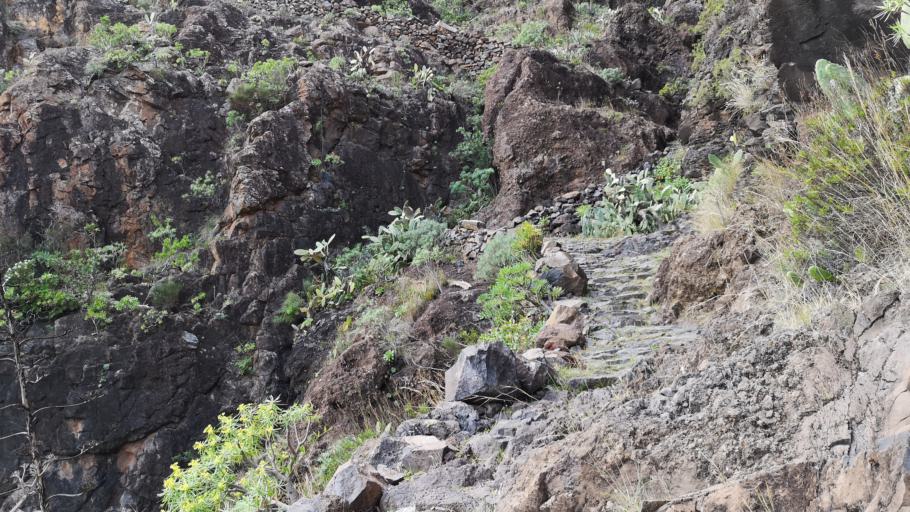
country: ES
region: Canary Islands
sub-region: Provincia de Santa Cruz de Tenerife
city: Alajero
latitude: 28.0628
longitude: -17.2249
